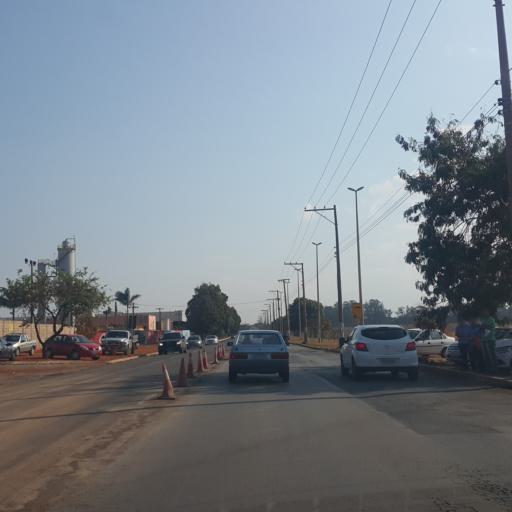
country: BR
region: Federal District
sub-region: Brasilia
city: Brasilia
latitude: -15.8690
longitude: -48.0382
